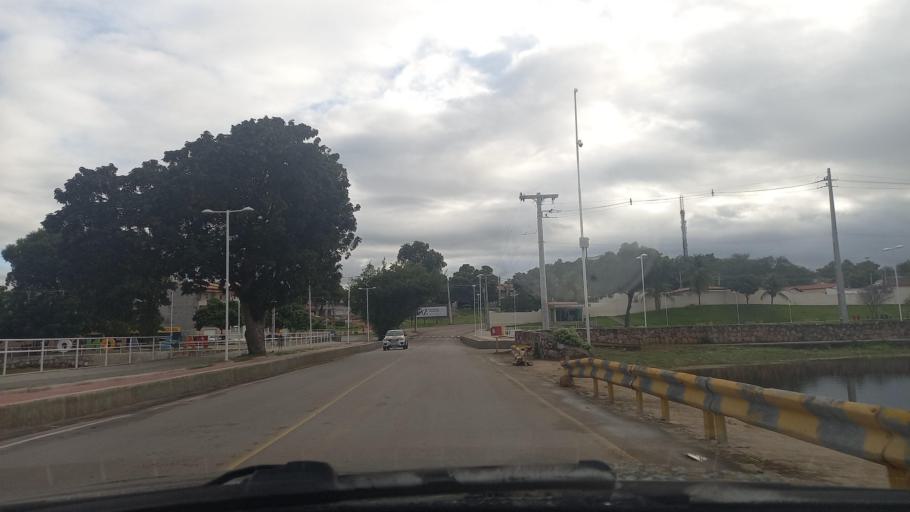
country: BR
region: Bahia
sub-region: Paulo Afonso
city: Paulo Afonso
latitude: -9.3965
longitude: -38.2128
